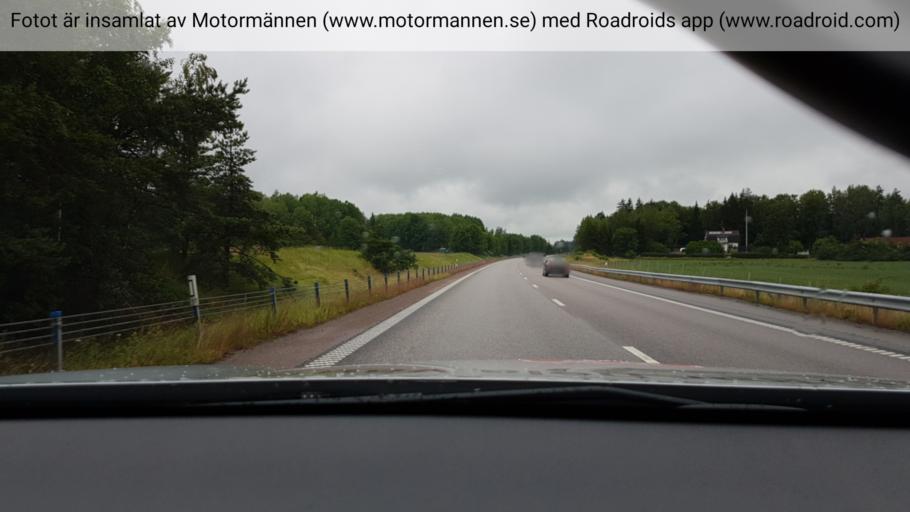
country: SE
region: Uppsala
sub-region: Uppsala Kommun
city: Alsike
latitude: 59.7780
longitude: 17.7817
